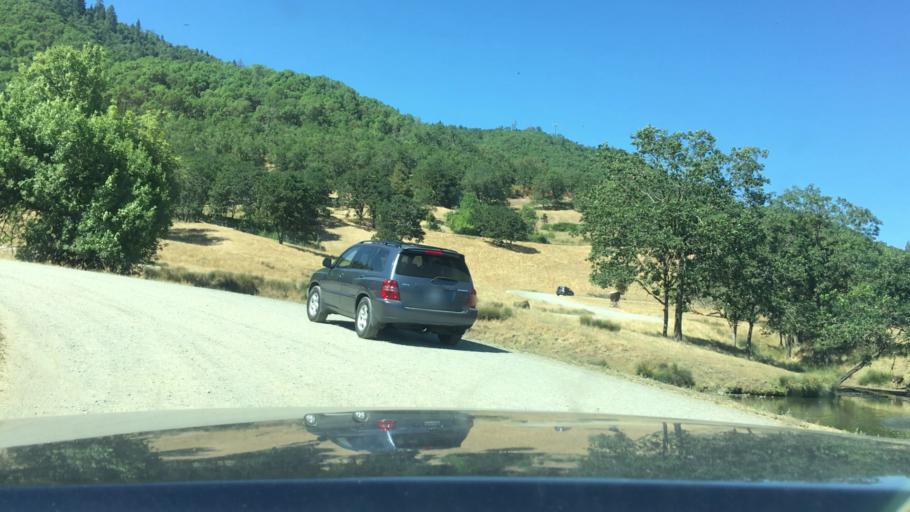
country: US
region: Oregon
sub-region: Douglas County
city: Winston
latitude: 43.1383
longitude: -123.4332
